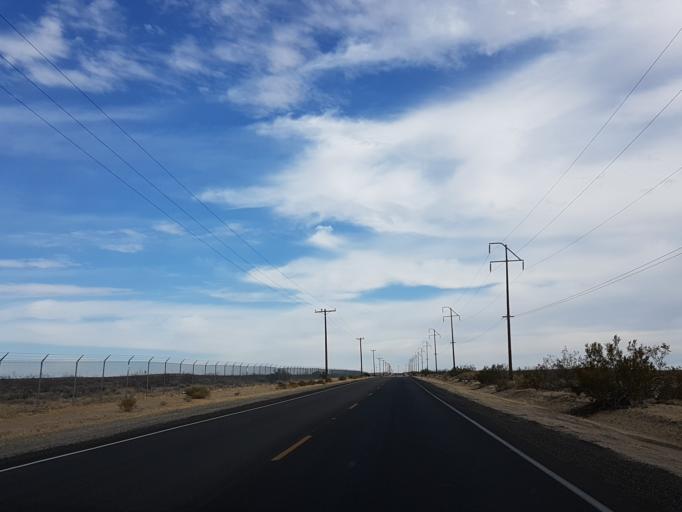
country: US
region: California
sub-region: Kern County
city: Ridgecrest
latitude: 35.6226
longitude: -117.6132
